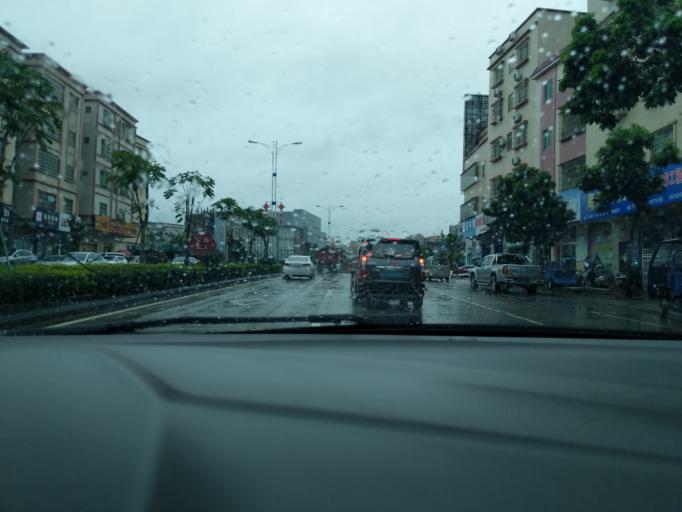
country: CN
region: Guangdong
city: Pingshi
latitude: 22.1978
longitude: 112.3323
